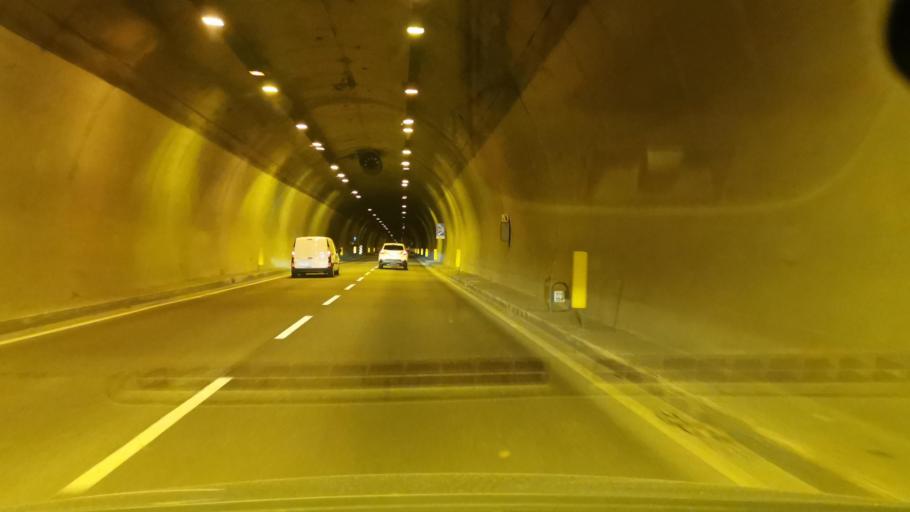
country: IT
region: Trentino-Alto Adige
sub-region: Provincia di Trento
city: Civezzano
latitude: 46.0827
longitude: 11.1742
